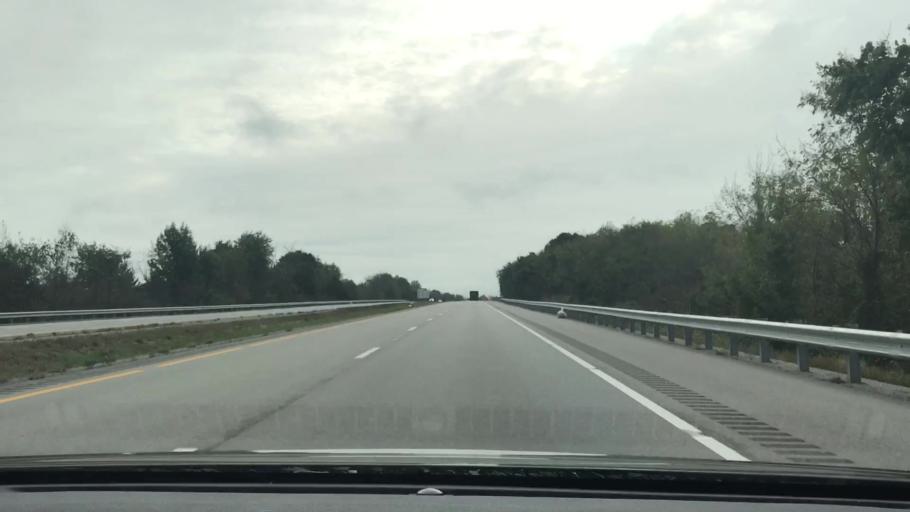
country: US
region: Kentucky
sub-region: Barren County
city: Cave City
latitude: 37.0476
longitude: -86.0833
